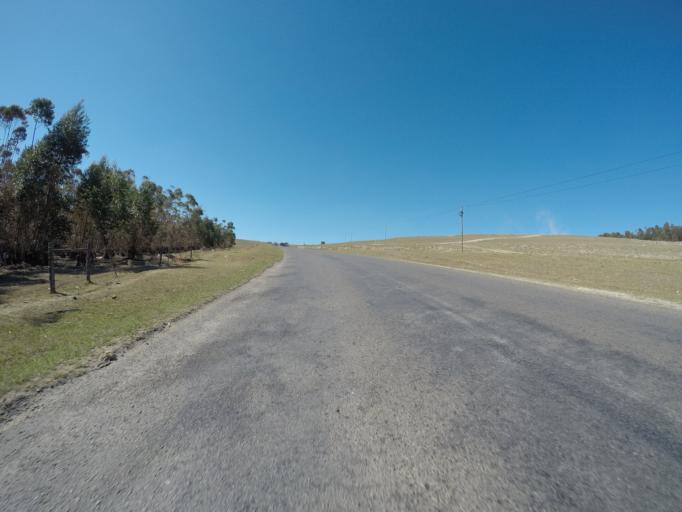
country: ZA
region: Eastern Cape
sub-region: OR Tambo District Municipality
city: Mthatha
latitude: -31.7781
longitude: 28.7372
